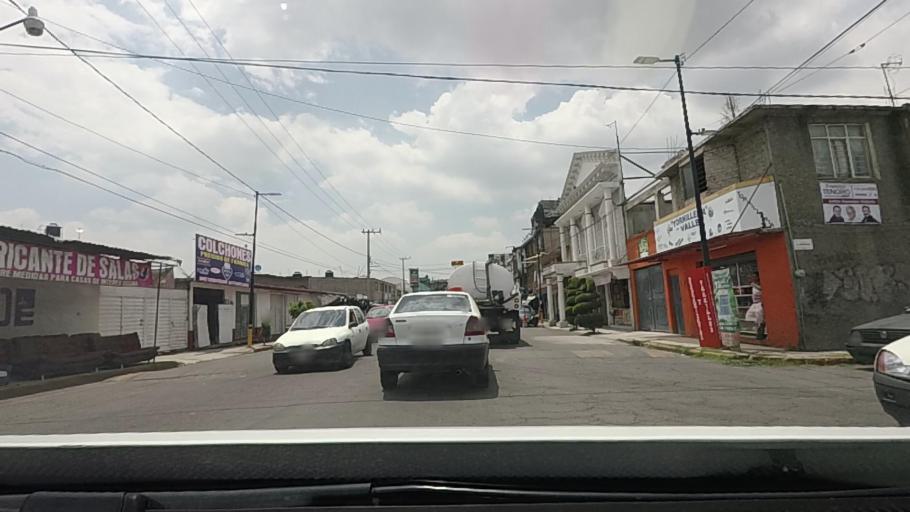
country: MX
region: Mexico
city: San Miguel Xico Viejo
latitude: 19.2893
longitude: -98.9176
